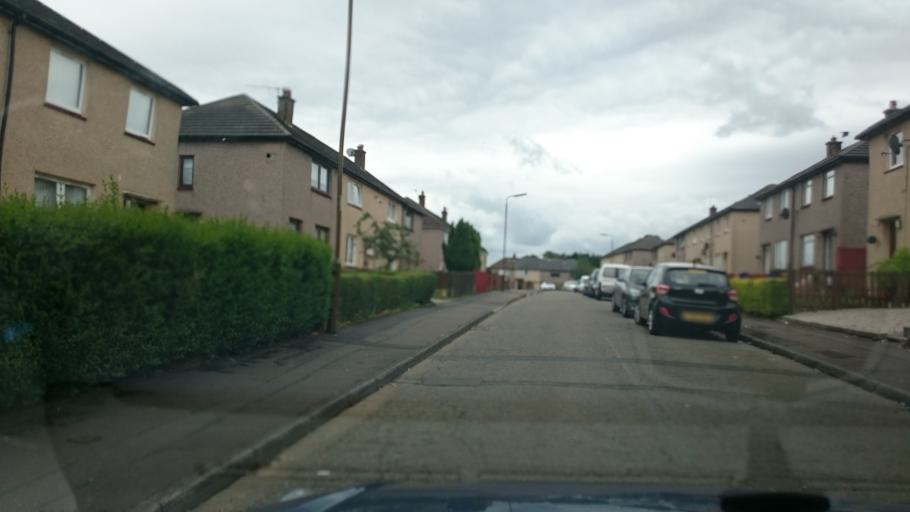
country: GB
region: Scotland
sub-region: Falkirk
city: Denny
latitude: 56.0046
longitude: -3.9102
